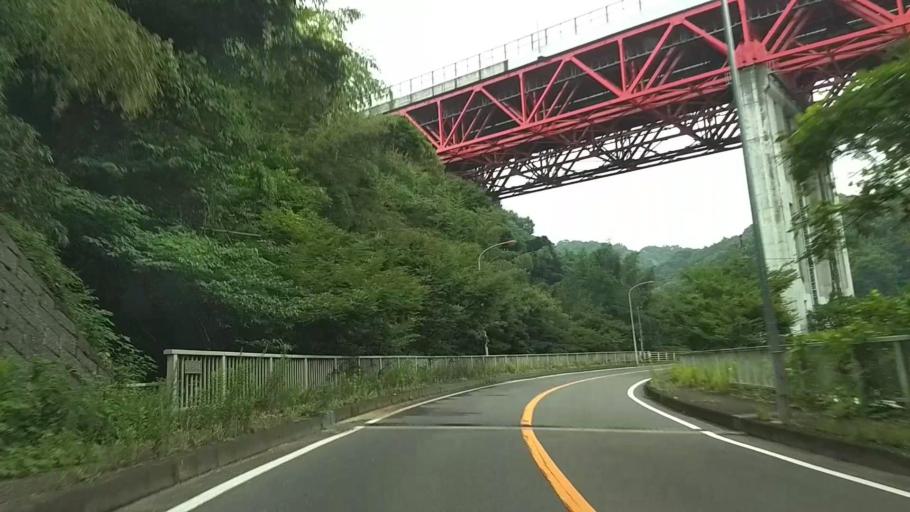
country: JP
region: Kanagawa
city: Hadano
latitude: 35.3398
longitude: 139.1948
